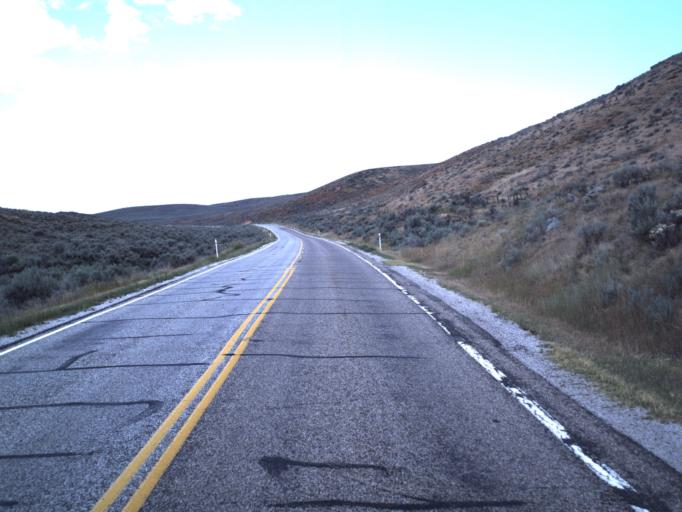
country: US
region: Utah
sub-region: Rich County
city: Randolph
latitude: 41.7850
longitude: -111.2063
